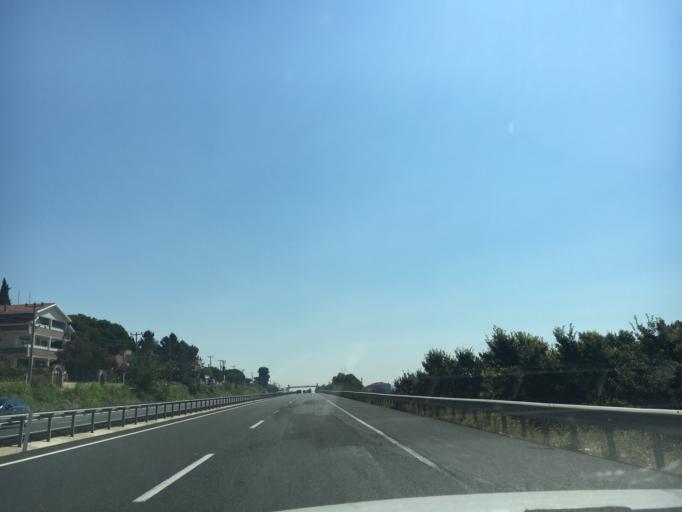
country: TR
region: Tekirdag
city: Marmara Ereglisi
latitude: 40.9695
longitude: 27.9036
